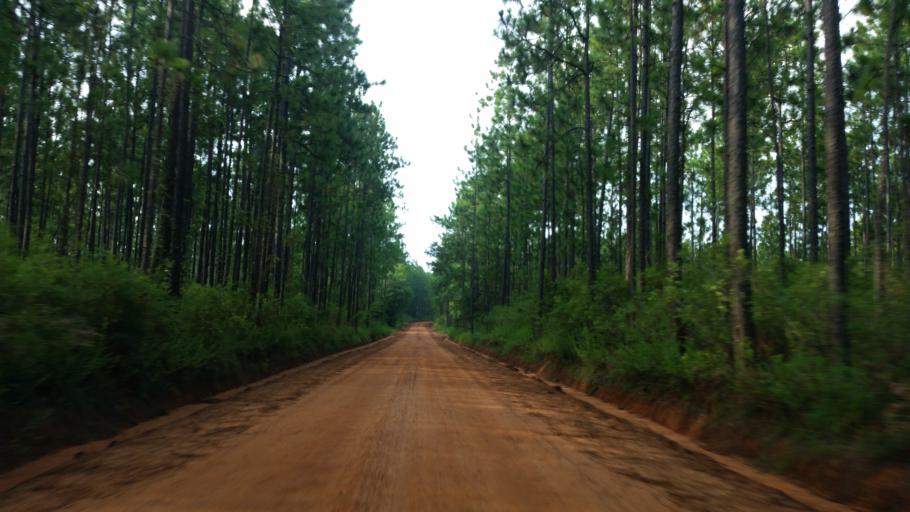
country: US
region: Alabama
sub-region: Escambia County
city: Atmore
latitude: 30.9471
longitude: -87.5716
